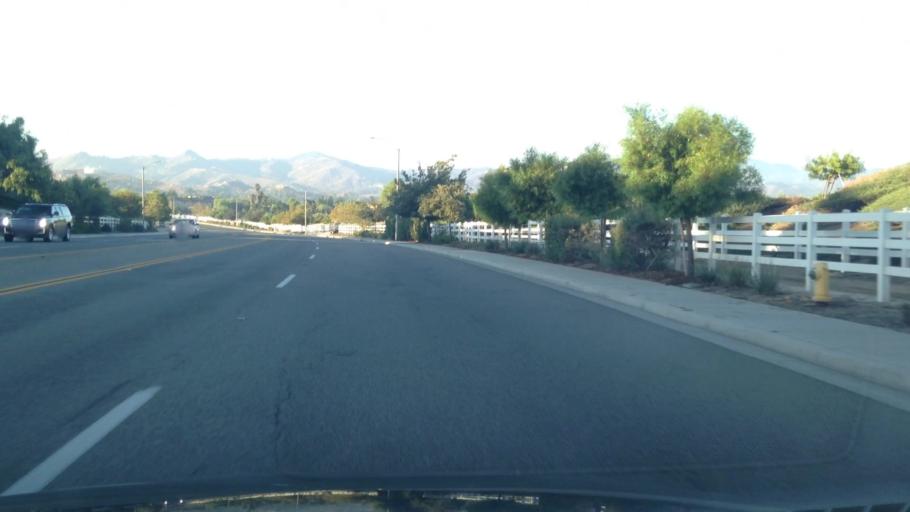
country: US
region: California
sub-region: Riverside County
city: Woodcrest
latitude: 33.8642
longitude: -117.3666
